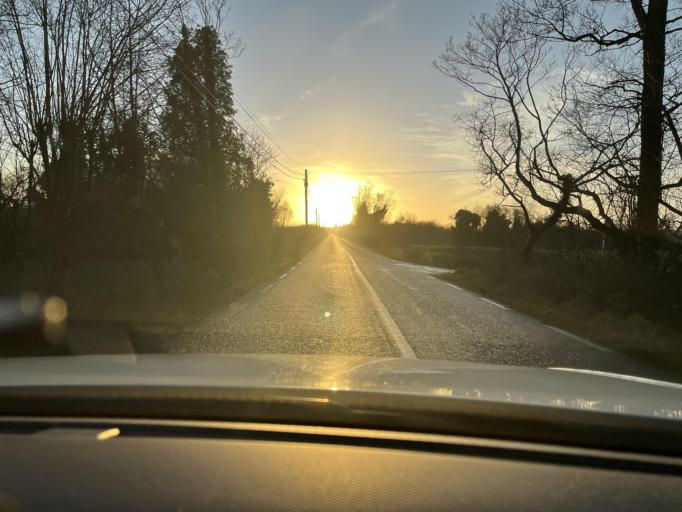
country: IE
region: Ulster
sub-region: An Cabhan
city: Ballyconnell
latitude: 54.1104
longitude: -7.5890
